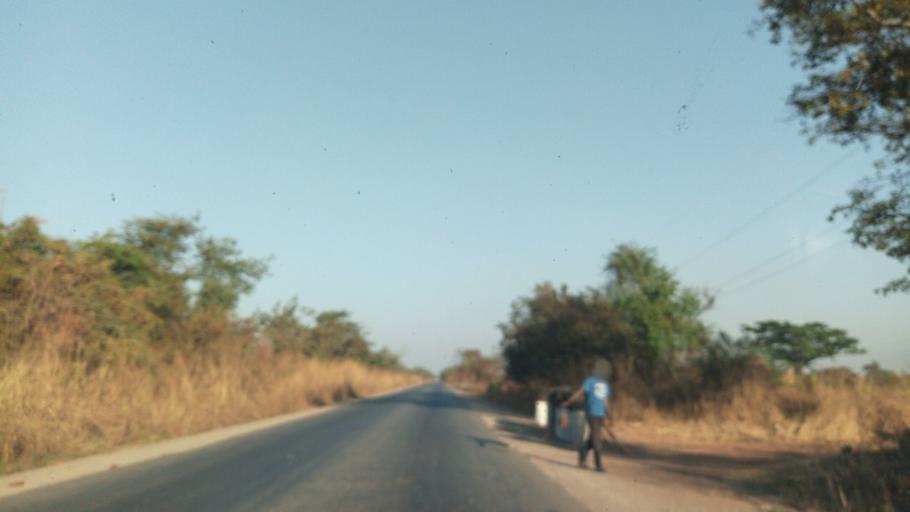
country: CD
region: Katanga
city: Likasi
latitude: -11.1134
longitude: 27.0250
